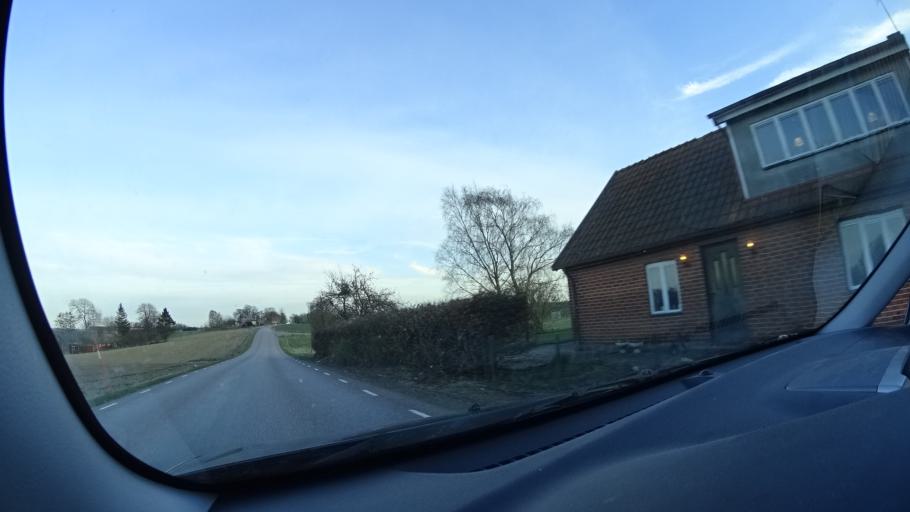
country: SE
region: Skane
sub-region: Eslovs Kommun
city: Stehag
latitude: 55.9195
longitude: 13.3822
